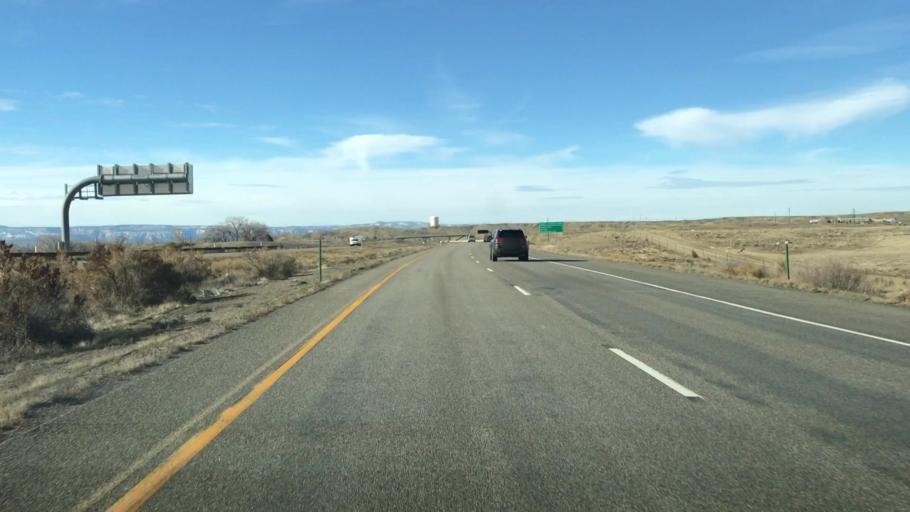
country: US
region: Colorado
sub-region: Mesa County
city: Clifton
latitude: 39.1078
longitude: -108.4313
